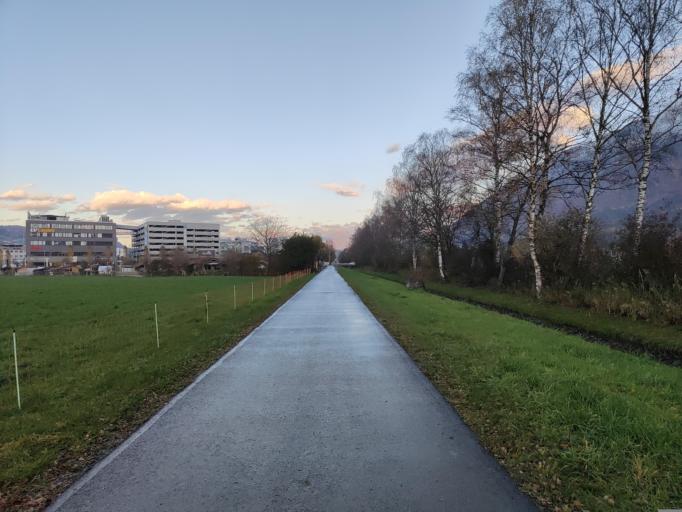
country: LI
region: Eschen
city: Eschen
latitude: 47.2042
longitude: 9.5317
